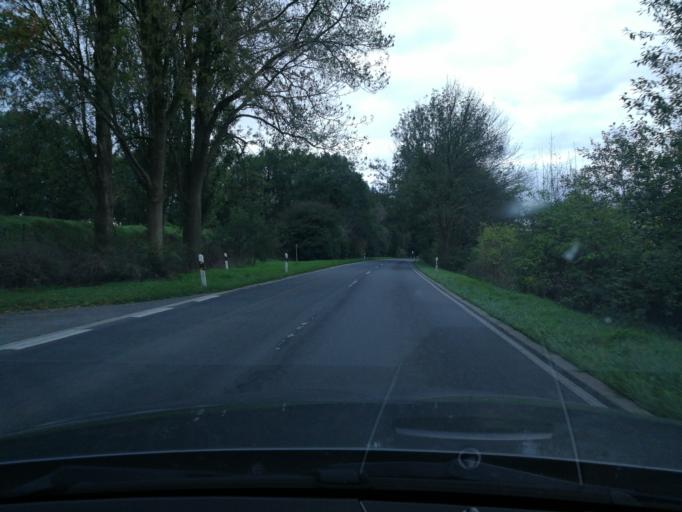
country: DE
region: North Rhine-Westphalia
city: Straelen
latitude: 51.4470
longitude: 6.2414
